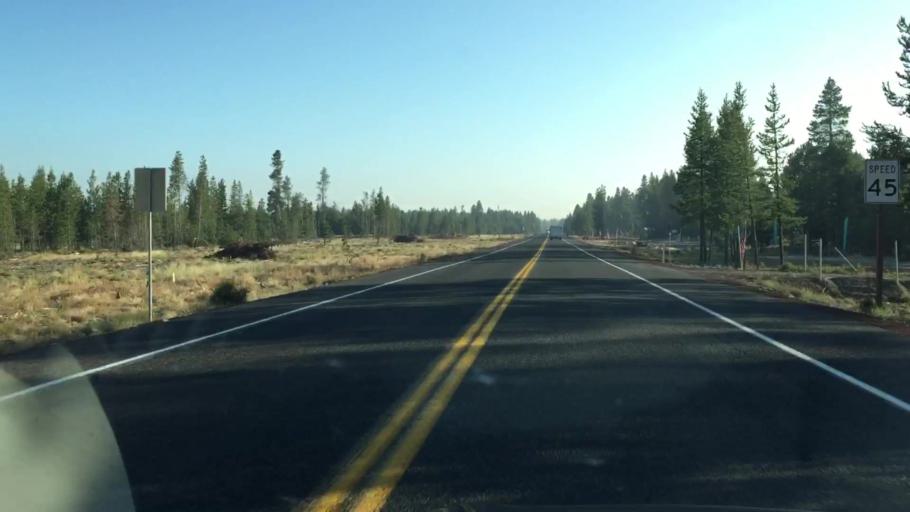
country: US
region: Oregon
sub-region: Deschutes County
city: La Pine
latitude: 43.4478
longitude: -121.7066
